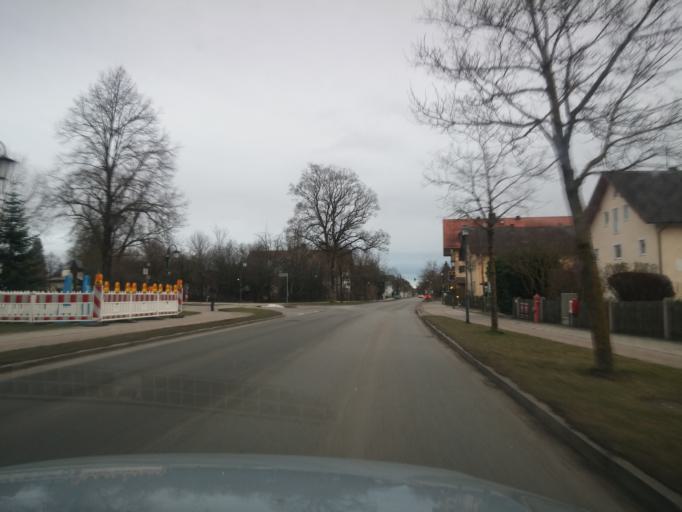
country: DE
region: Bavaria
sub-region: Upper Bavaria
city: Aschheim
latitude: 48.1746
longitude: 11.7147
